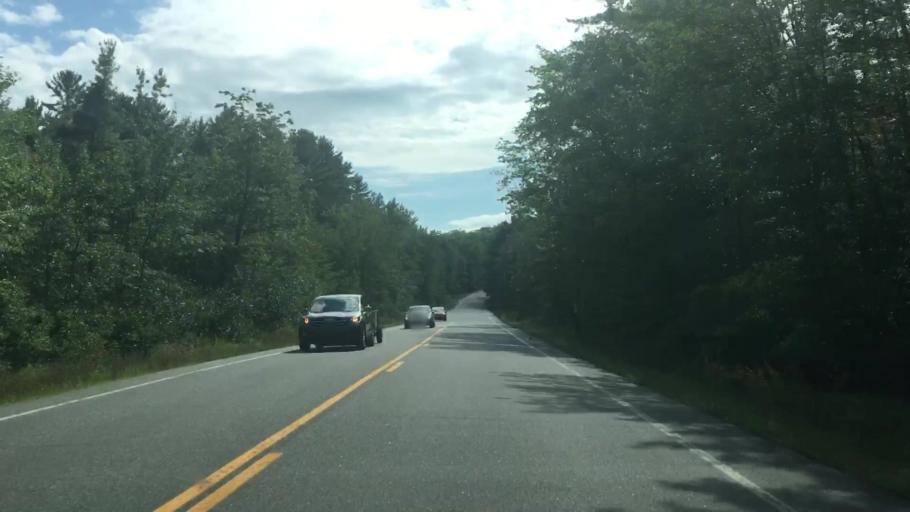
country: US
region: Maine
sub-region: Androscoggin County
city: Poland
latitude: 44.0199
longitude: -70.4413
